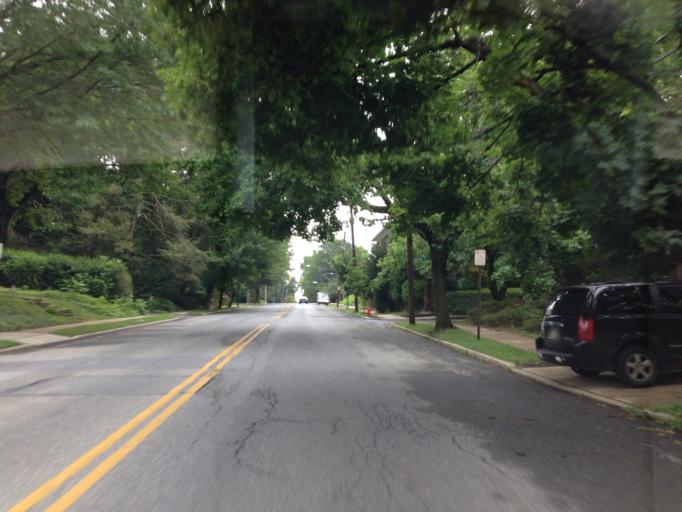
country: US
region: Pennsylvania
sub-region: Lancaster County
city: Lancaster
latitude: 40.0427
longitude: -76.3247
